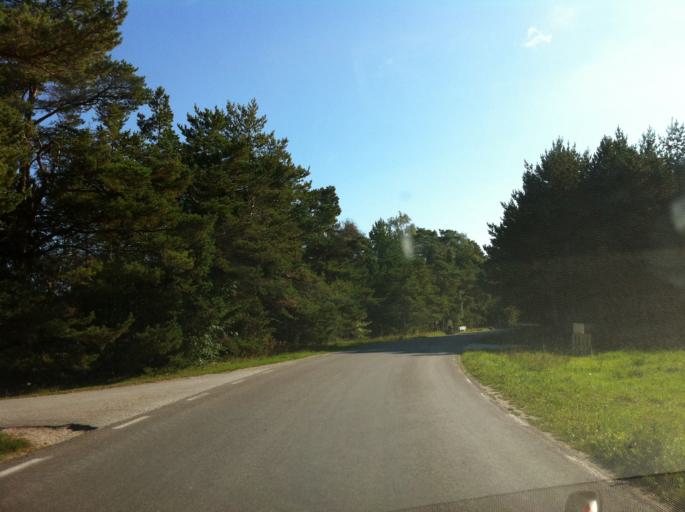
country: SE
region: Gotland
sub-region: Gotland
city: Slite
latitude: 57.9663
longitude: 19.2364
